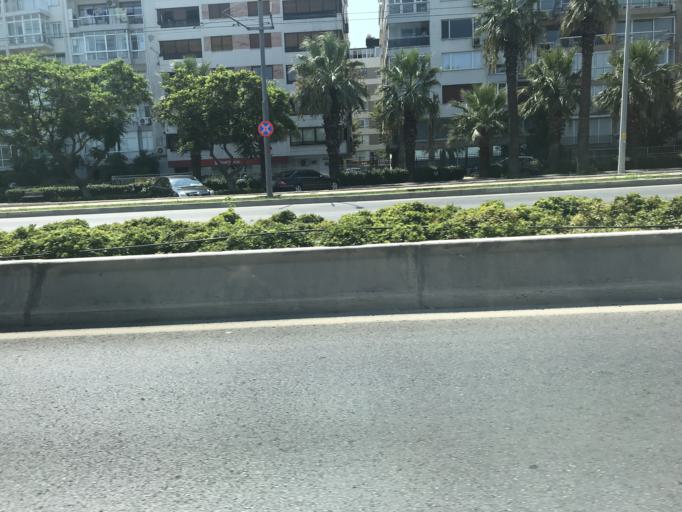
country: TR
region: Izmir
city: Izmir
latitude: 38.3988
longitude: 27.0884
